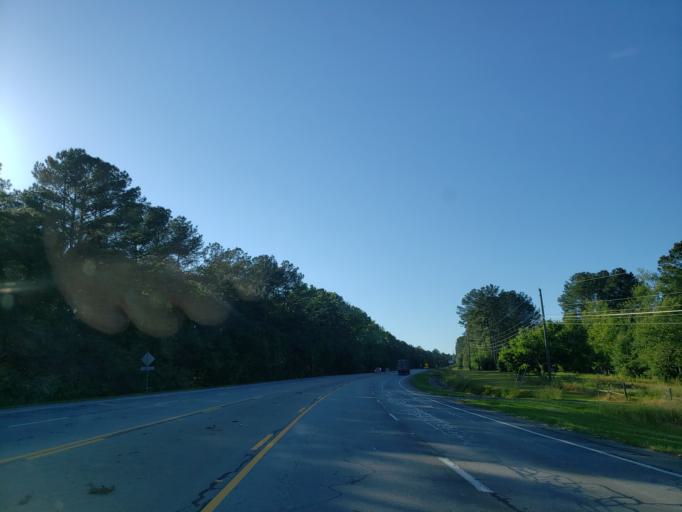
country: US
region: Georgia
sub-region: Haralson County
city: Buchanan
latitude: 33.8189
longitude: -85.2025
